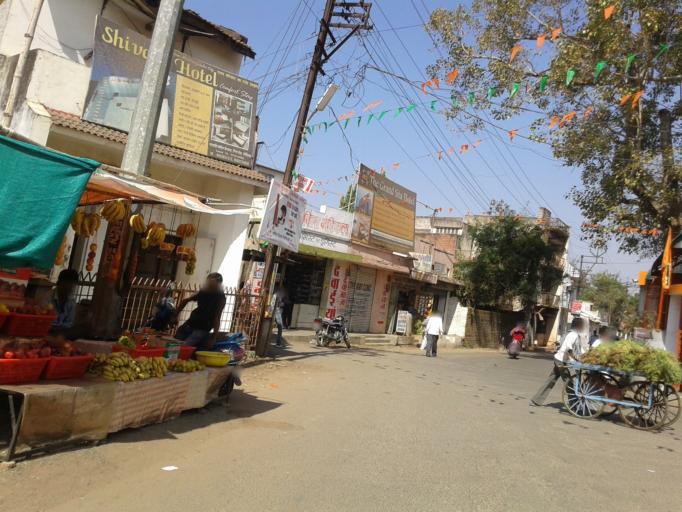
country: IN
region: Maharashtra
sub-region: Gondiya
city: Gondia
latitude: 21.4641
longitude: 80.1894
